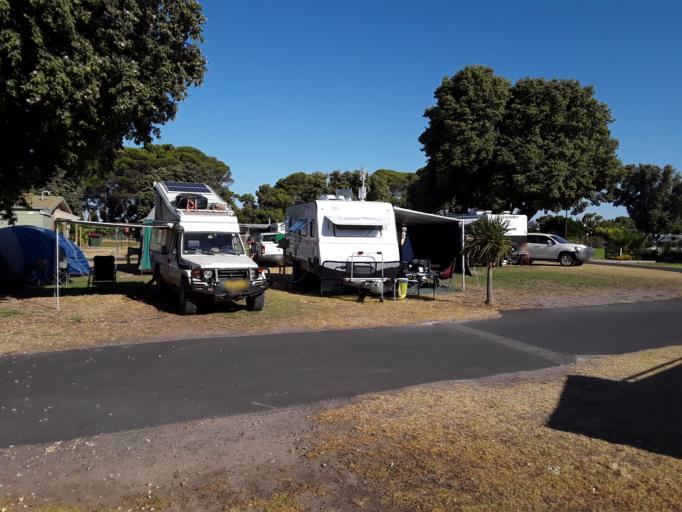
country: AU
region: South Australia
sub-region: Tatiara
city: Keith
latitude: -36.8369
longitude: 139.8456
